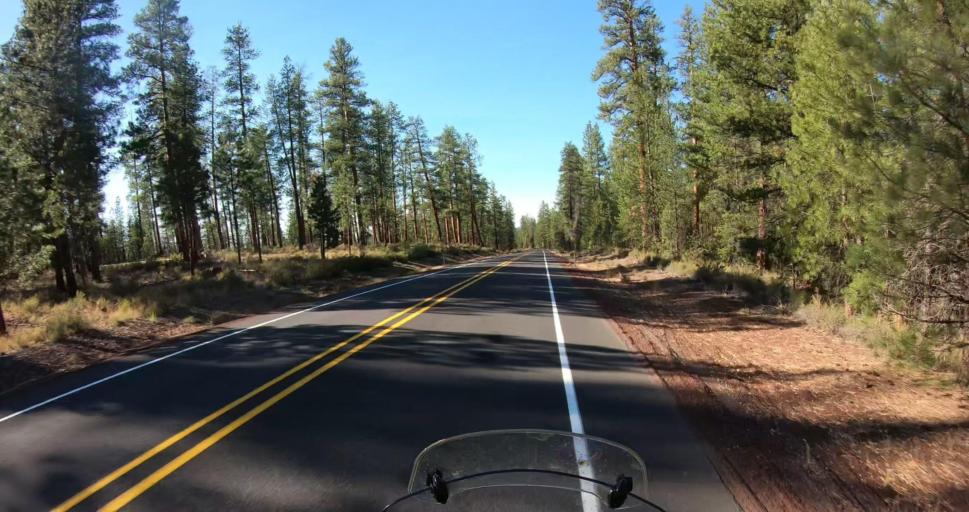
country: US
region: Oregon
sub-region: Deschutes County
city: La Pine
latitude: 43.4698
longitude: -121.3988
